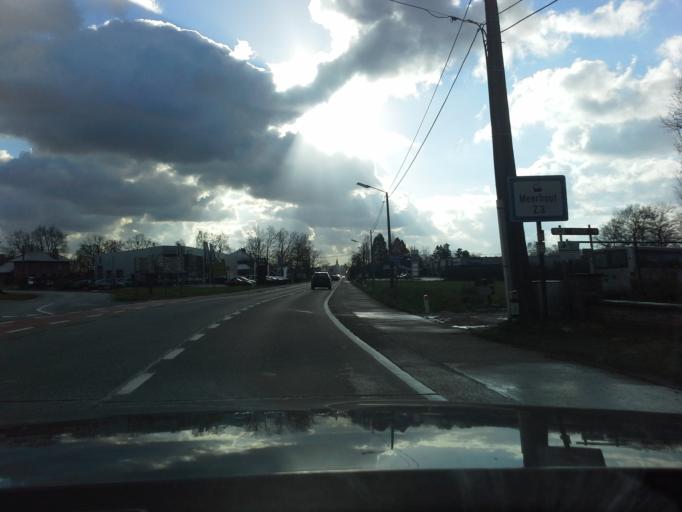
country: BE
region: Flanders
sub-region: Provincie Antwerpen
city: Meerhout
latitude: 51.1448
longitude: 5.0877
